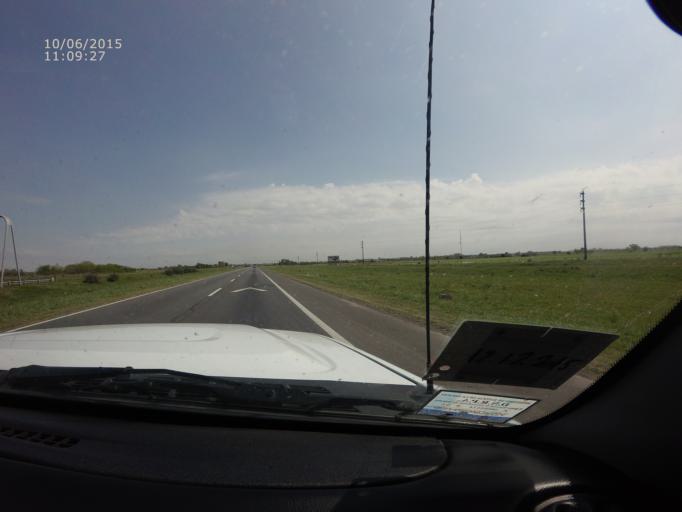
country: AR
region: Santa Fe
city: Arroyo Seco
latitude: -33.1637
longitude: -60.5355
